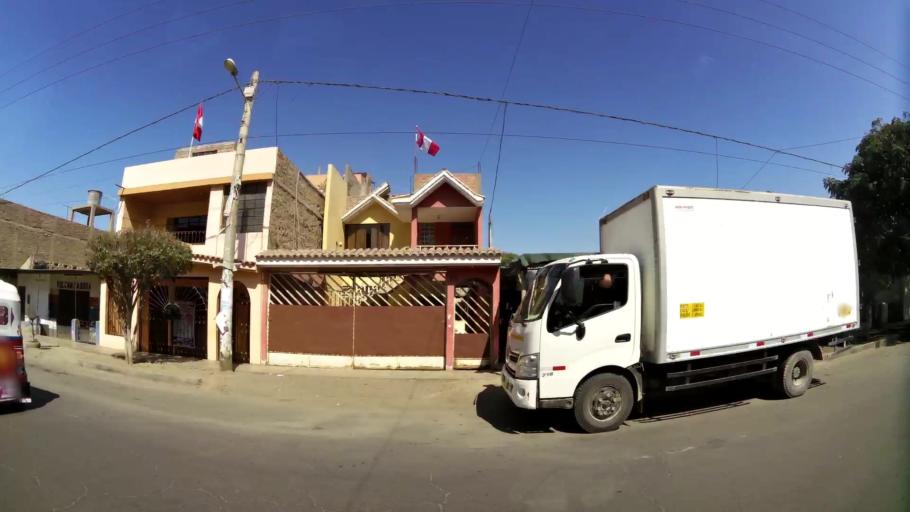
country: PE
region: Ica
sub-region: Provincia de Ica
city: La Tinguina
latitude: -14.0463
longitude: -75.7072
